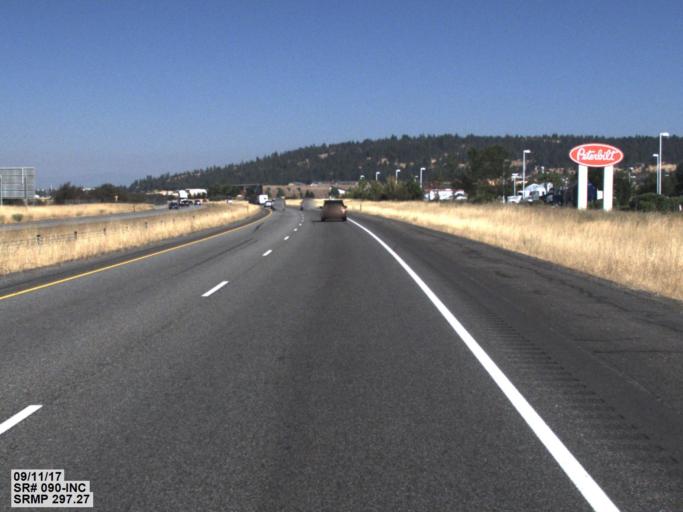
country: US
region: Washington
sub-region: Spokane County
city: Liberty Lake
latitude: 47.6805
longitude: -117.0903
